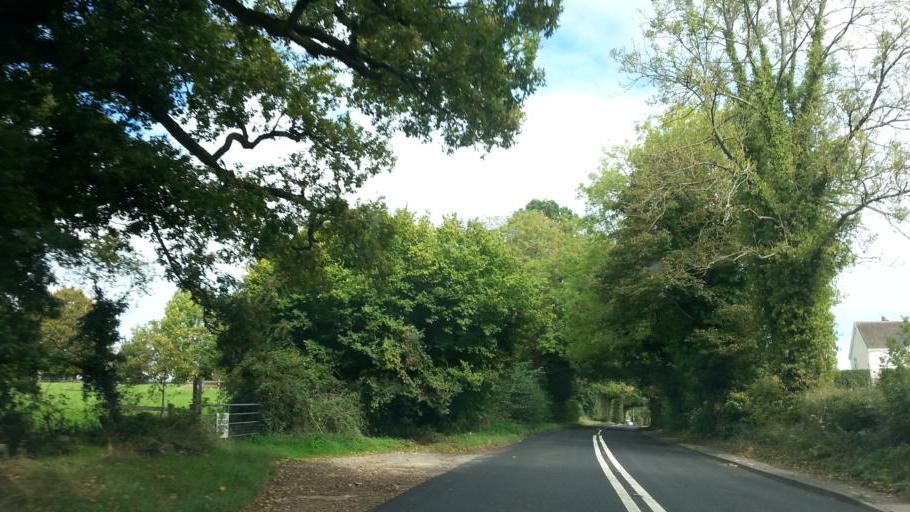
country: GB
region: England
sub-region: Gloucestershire
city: Painswick
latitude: 51.7803
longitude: -2.2047
